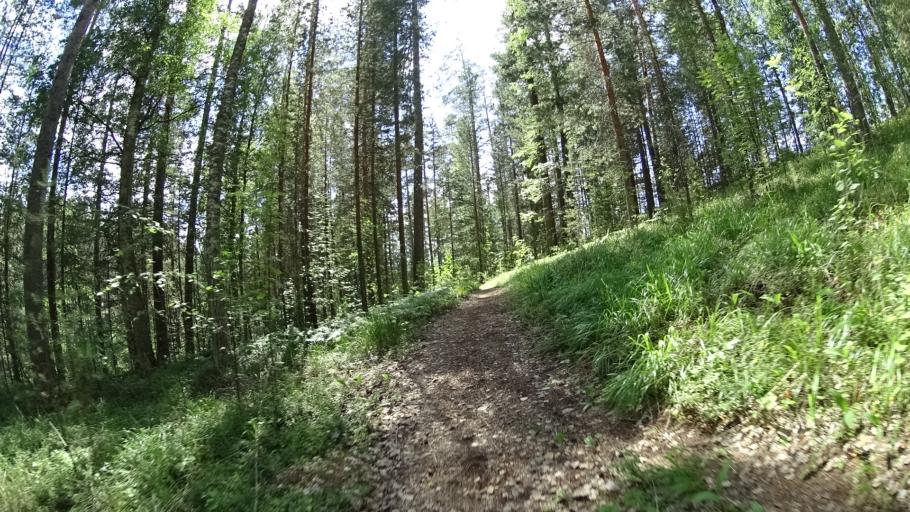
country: FI
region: Southern Savonia
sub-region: Savonlinna
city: Punkaharju
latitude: 61.7936
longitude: 29.3036
